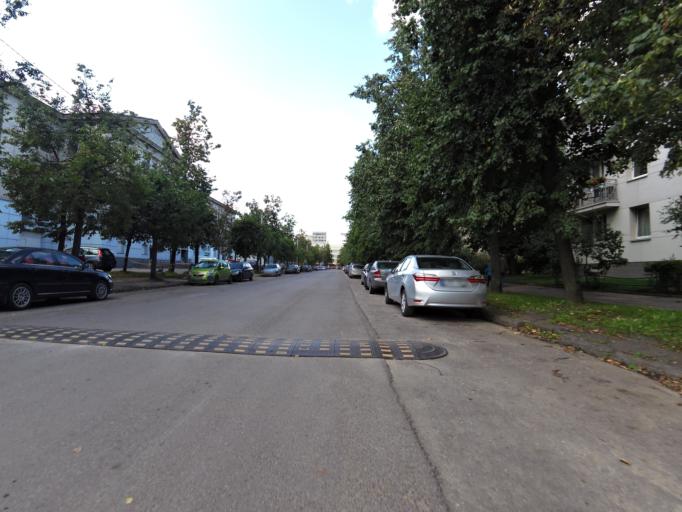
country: LT
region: Vilnius County
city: Naujamiestis
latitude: 54.6749
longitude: 25.2617
